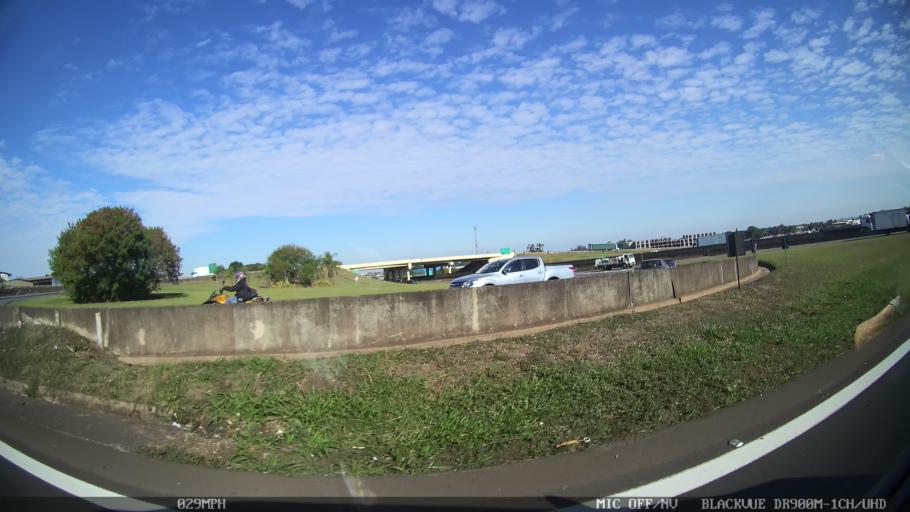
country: BR
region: Sao Paulo
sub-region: Nova Odessa
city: Nova Odessa
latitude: -22.7525
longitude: -47.2578
